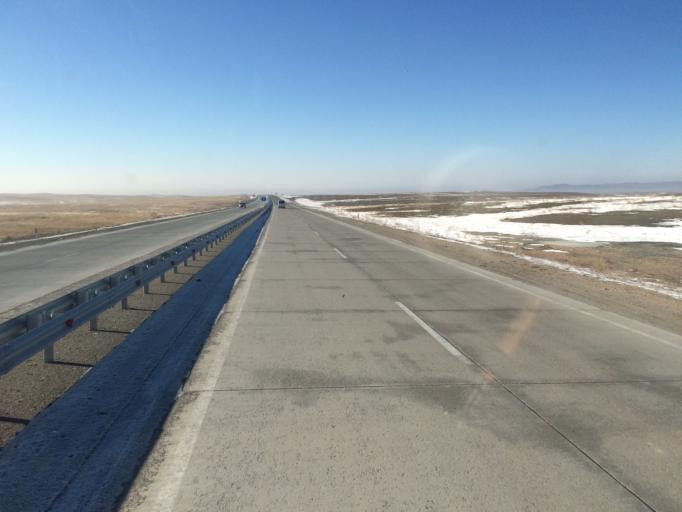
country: KZ
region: Zhambyl
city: Georgiyevka
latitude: 43.3593
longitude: 74.6286
